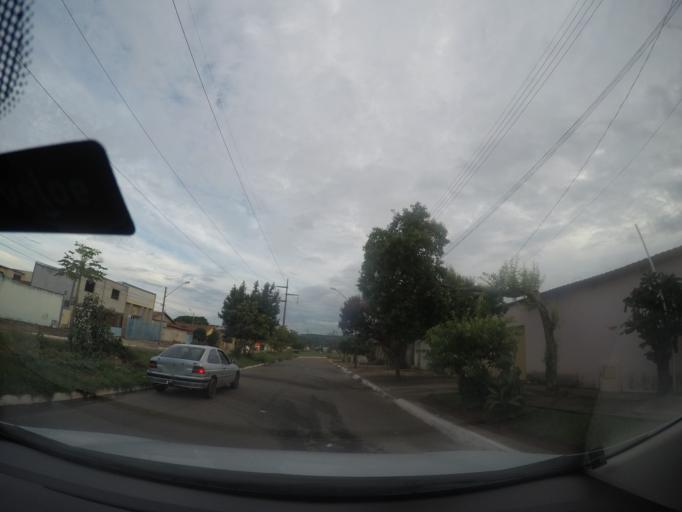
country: BR
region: Goias
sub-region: Goianira
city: Goianira
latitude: -16.5918
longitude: -49.3754
